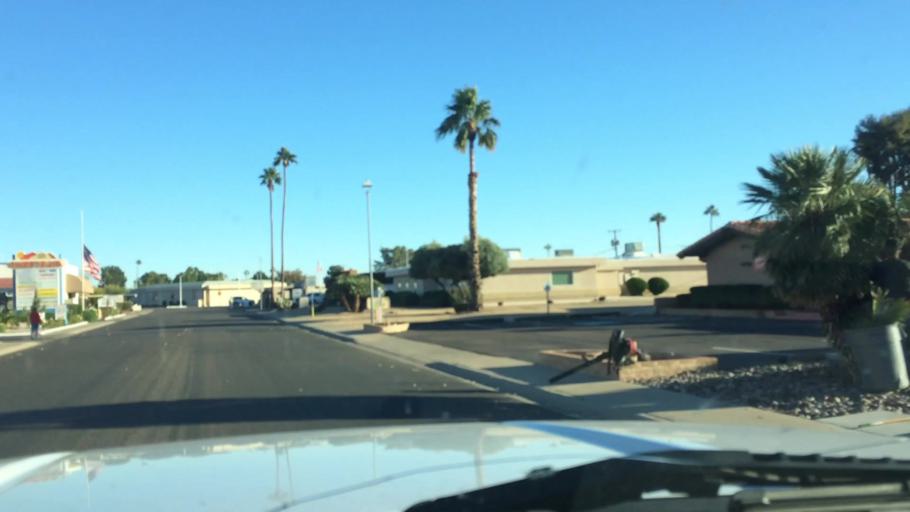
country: US
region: Arizona
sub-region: Maricopa County
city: Sun City
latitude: 33.5993
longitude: -112.2838
